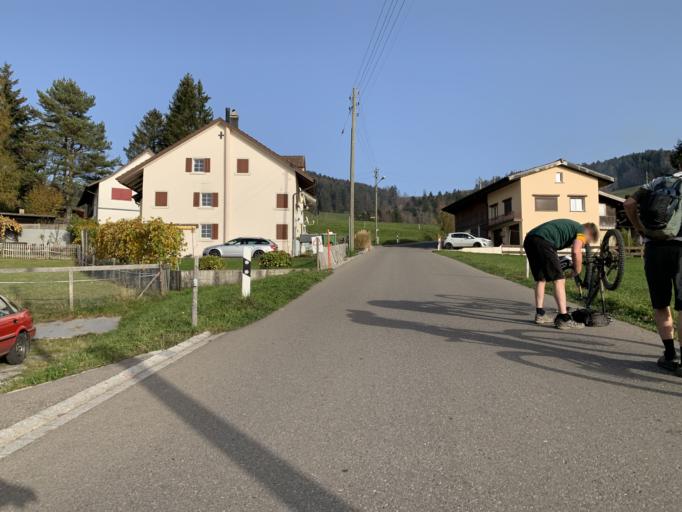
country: CH
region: Zurich
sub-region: Bezirk Hinwil
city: Hadlikon
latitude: 47.3052
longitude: 8.8738
